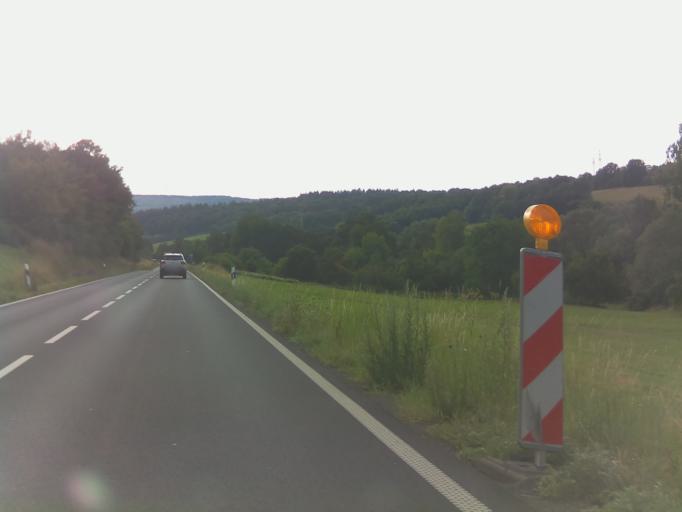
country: DE
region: Hesse
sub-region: Regierungsbezirk Darmstadt
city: Bad Orb
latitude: 50.2359
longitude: 9.3248
